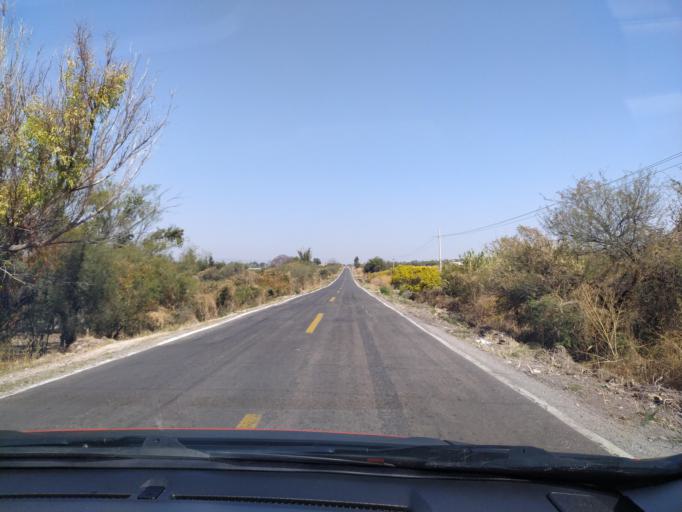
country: MX
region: Guanajuato
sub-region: San Francisco del Rincon
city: San Ignacio de Hidalgo
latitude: 20.8075
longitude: -101.8375
